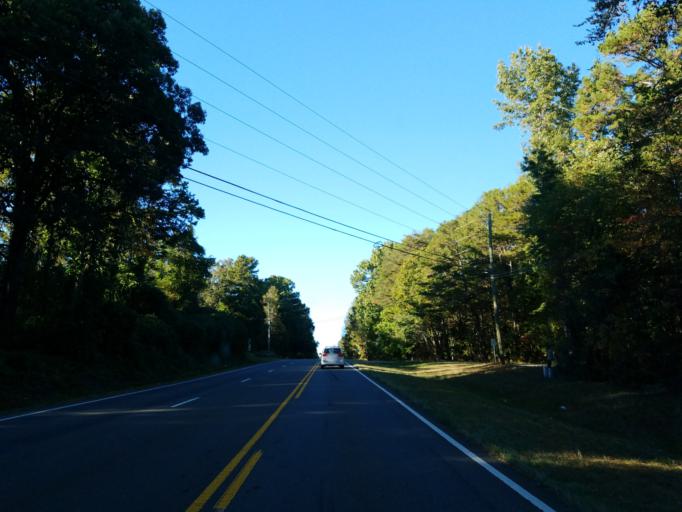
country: US
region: Georgia
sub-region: Pickens County
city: Nelson
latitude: 34.4037
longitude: -84.3846
